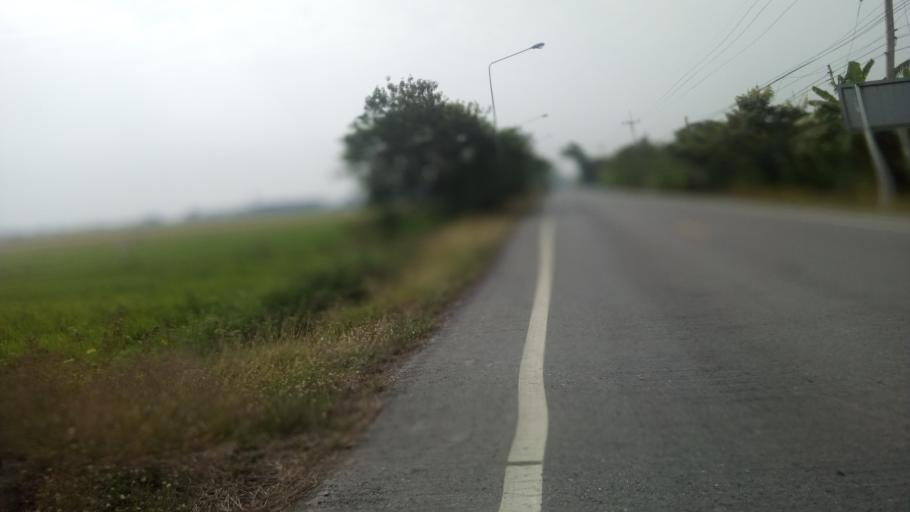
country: TH
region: Pathum Thani
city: Ban Rangsit
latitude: 14.0321
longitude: 100.8245
